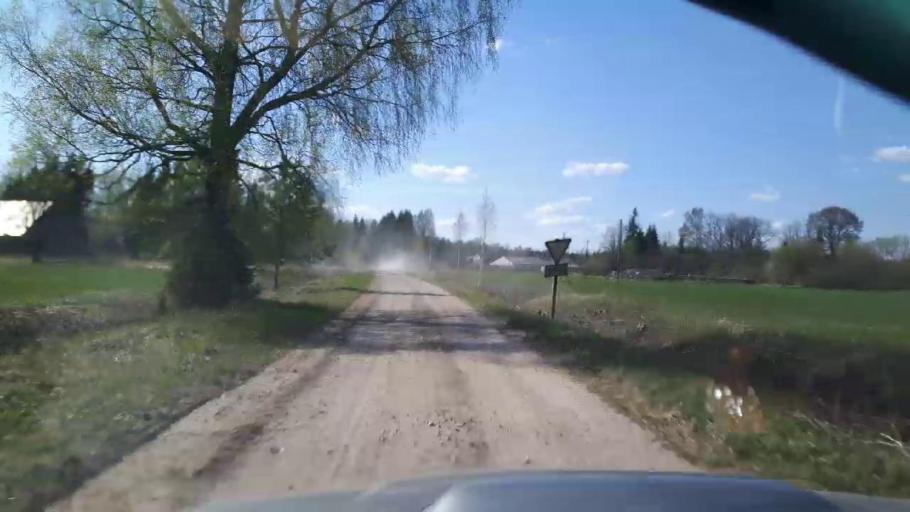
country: EE
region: Paernumaa
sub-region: Tootsi vald
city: Tootsi
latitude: 58.4488
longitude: 24.8616
